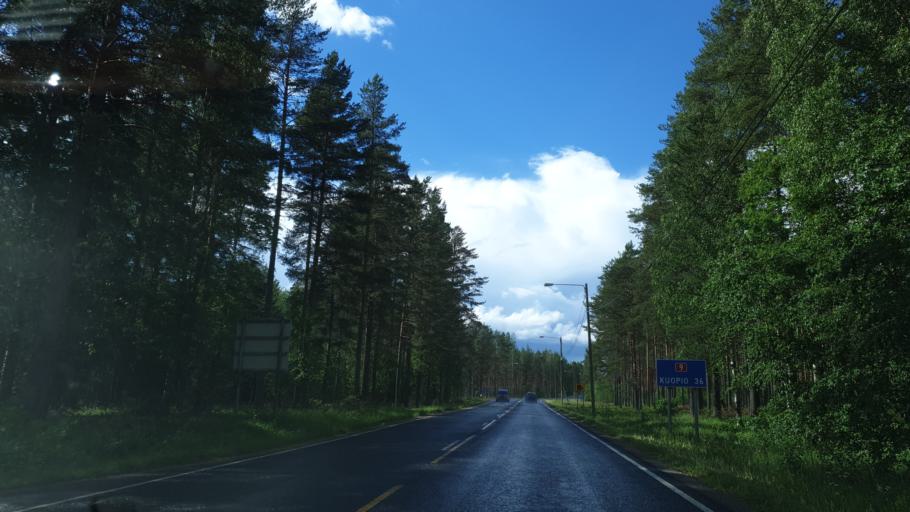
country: FI
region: Northern Savo
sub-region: Kuopio
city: Vehmersalmi
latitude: 62.9118
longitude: 28.1524
